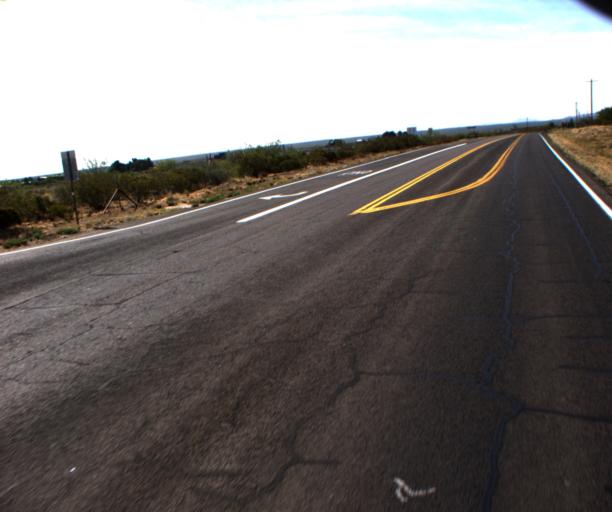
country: US
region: Arizona
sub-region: Graham County
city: Swift Trail Junction
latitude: 32.7154
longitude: -109.7085
